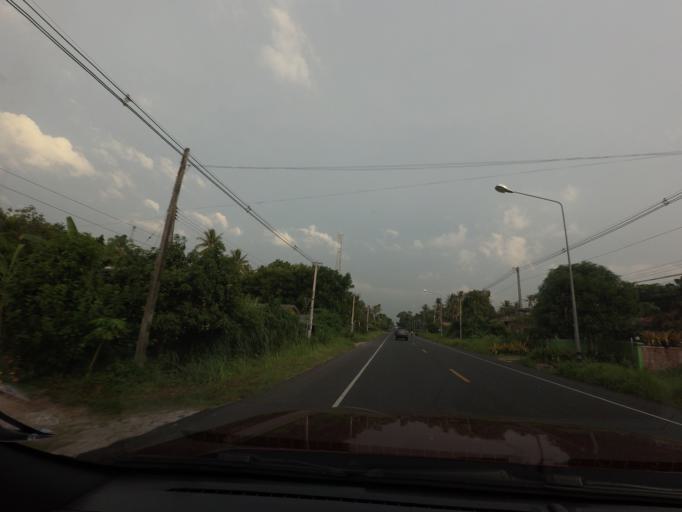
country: TH
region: Pattani
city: Mae Lan
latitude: 6.6120
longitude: 101.1910
